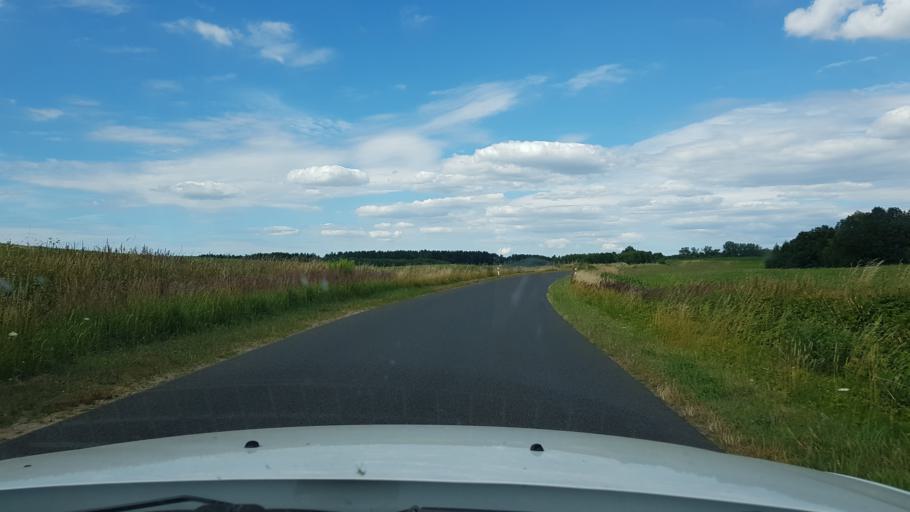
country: PL
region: West Pomeranian Voivodeship
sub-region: Powiat drawski
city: Kalisz Pomorski
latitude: 53.3857
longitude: 15.9473
